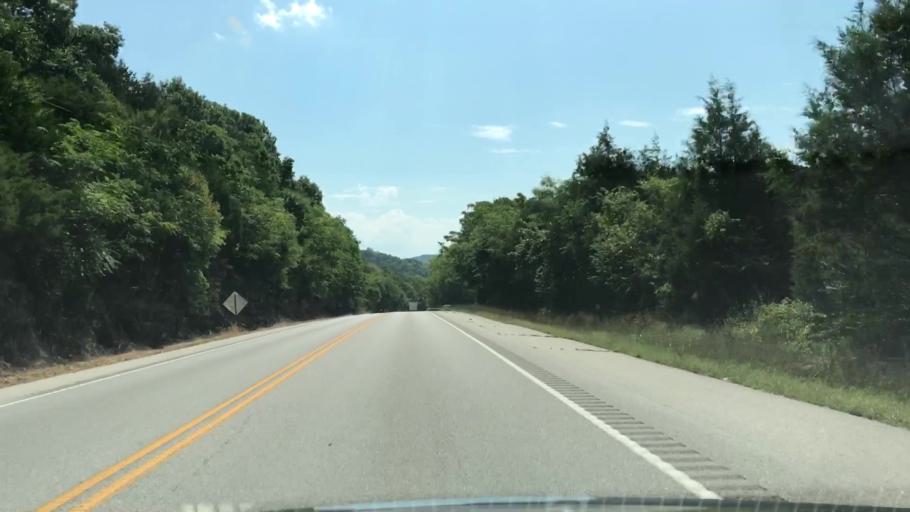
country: US
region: Tennessee
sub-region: Smith County
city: Carthage
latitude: 36.3218
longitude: -86.0165
